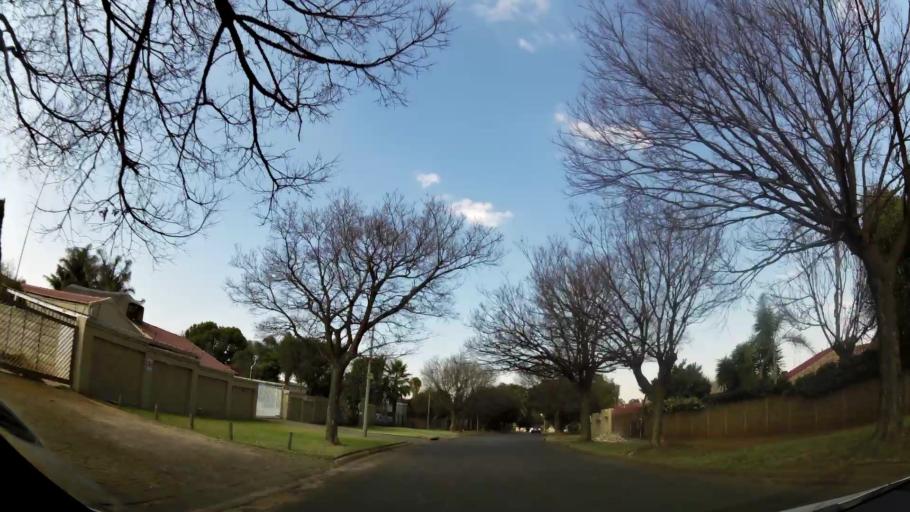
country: ZA
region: Gauteng
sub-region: Ekurhuleni Metropolitan Municipality
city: Boksburg
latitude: -26.1915
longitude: 28.2362
